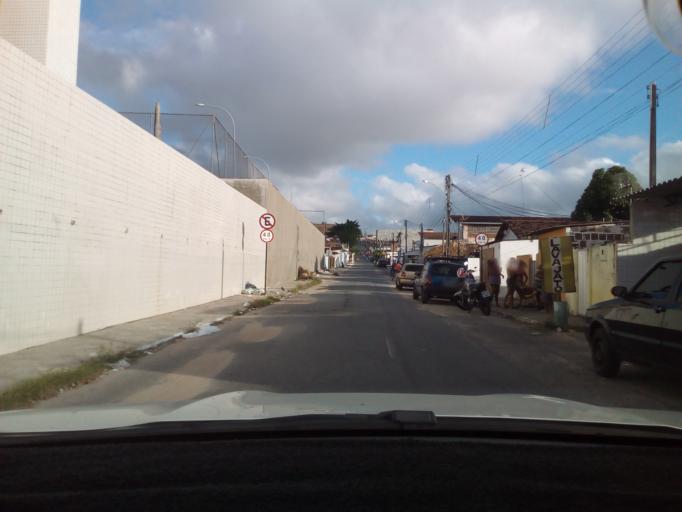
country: BR
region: Paraiba
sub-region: Joao Pessoa
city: Joao Pessoa
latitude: -7.1025
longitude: -34.8599
